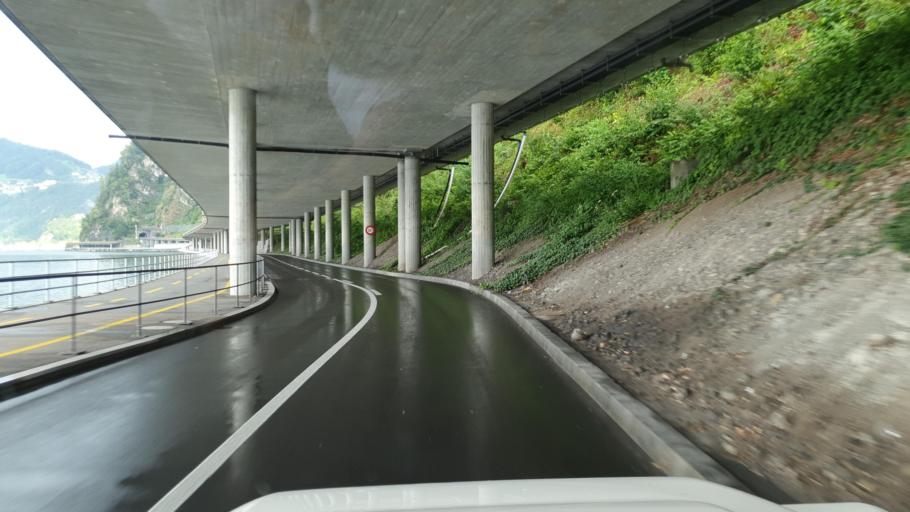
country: CH
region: Nidwalden
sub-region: Nidwalden
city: Hergiswil
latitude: 46.9788
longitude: 8.3145
